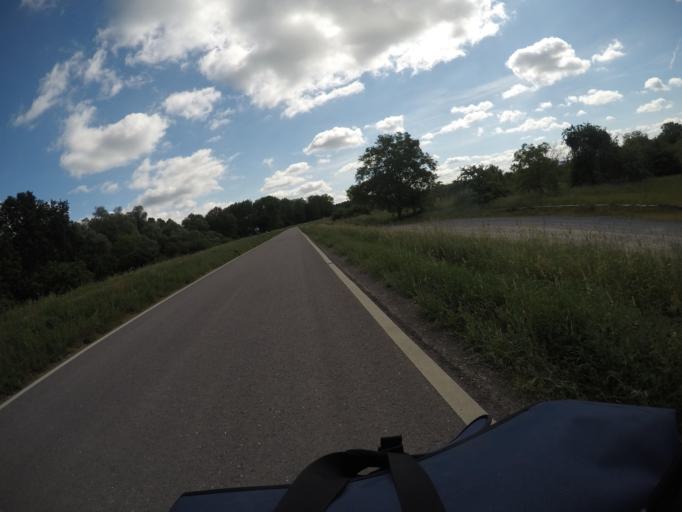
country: DE
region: Baden-Wuerttemberg
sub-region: Karlsruhe Region
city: Au am Rhein
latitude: 48.9568
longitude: 8.2183
